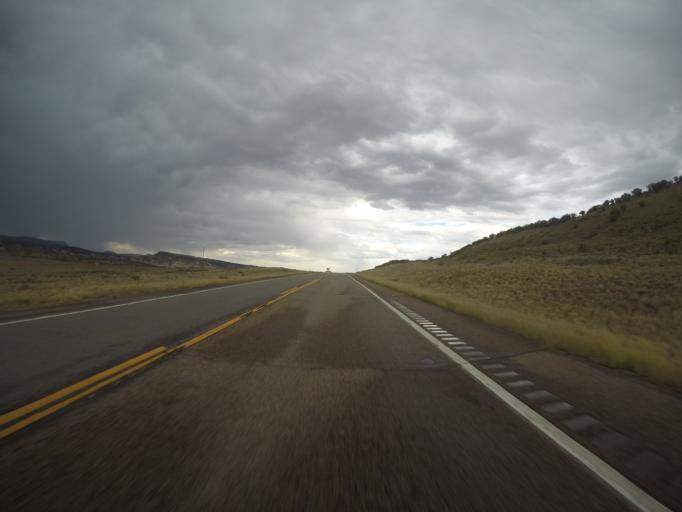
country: US
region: Colorado
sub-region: Rio Blanco County
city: Rangely
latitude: 40.2514
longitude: -108.8187
